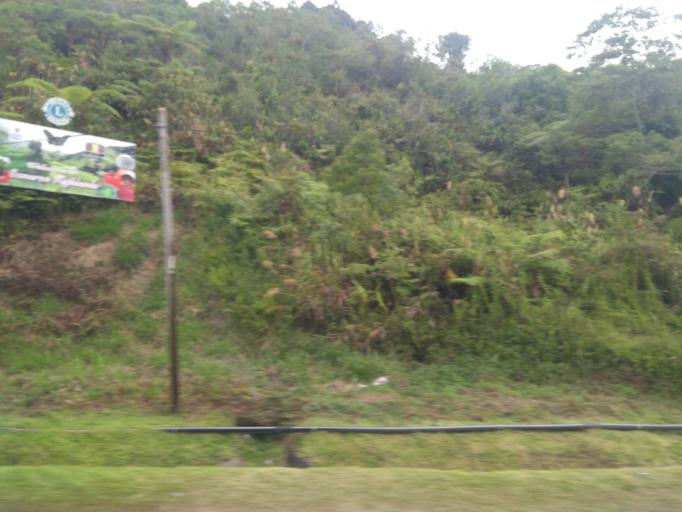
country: MY
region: Pahang
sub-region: Cameron Highlands
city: Tanah Rata
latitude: 4.5829
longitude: 101.4159
